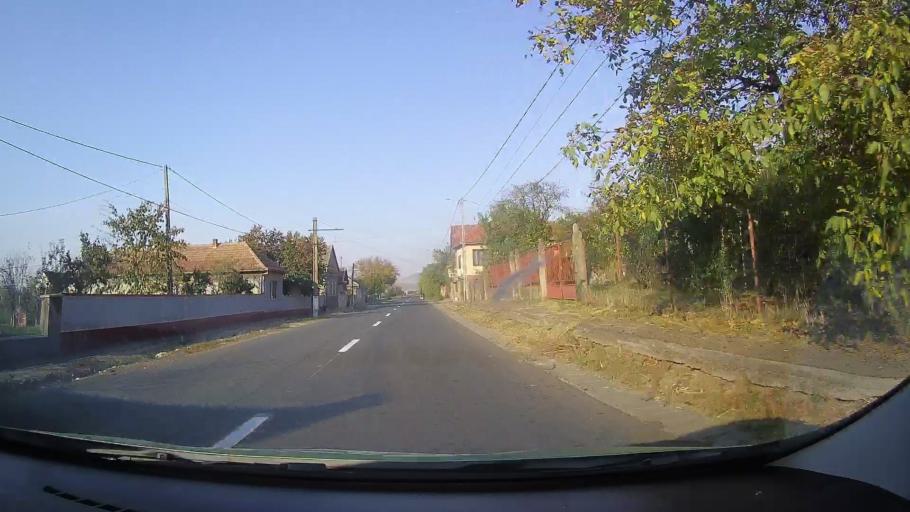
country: RO
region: Arad
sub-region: Comuna Covasint
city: Covasint
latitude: 46.2086
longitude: 21.6101
